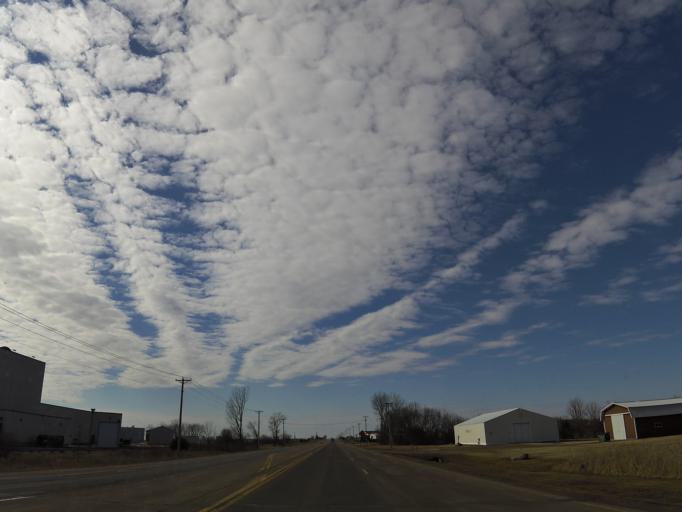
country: US
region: Minnesota
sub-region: Waseca County
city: Waseca
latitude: 44.0824
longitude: -93.5373
